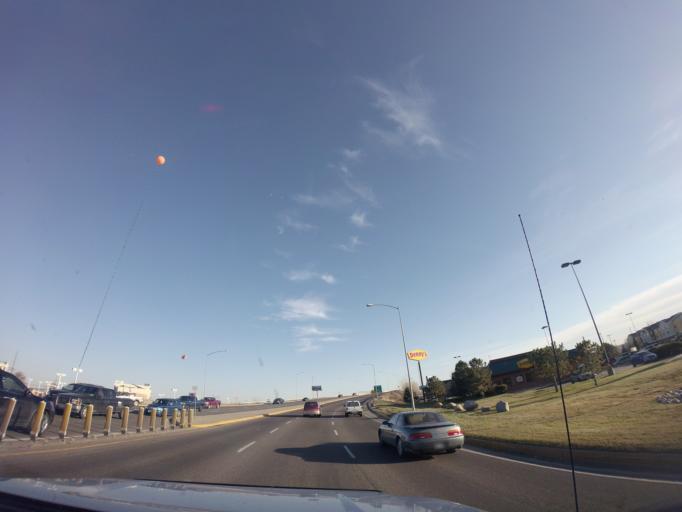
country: US
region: Montana
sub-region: Yellowstone County
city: Billings
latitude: 45.7541
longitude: -108.5641
